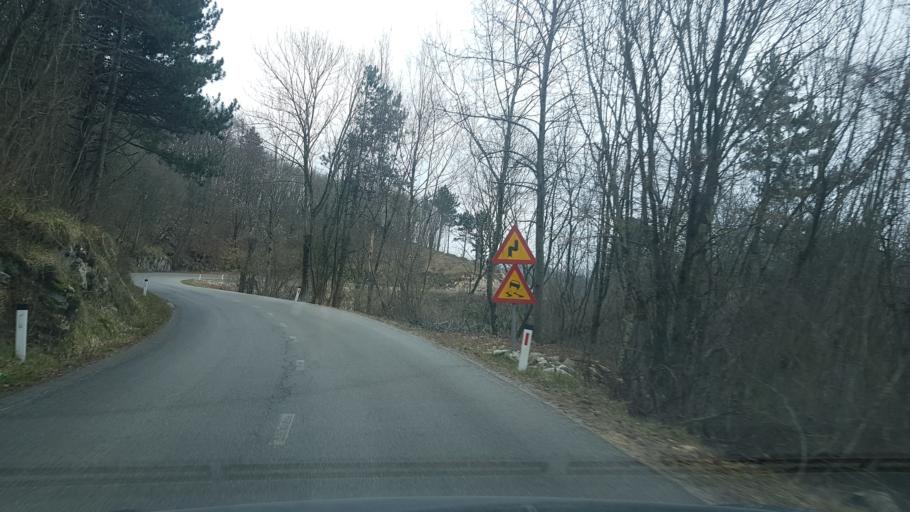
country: SI
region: Kanal
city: Kanal
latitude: 46.0417
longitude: 13.6720
